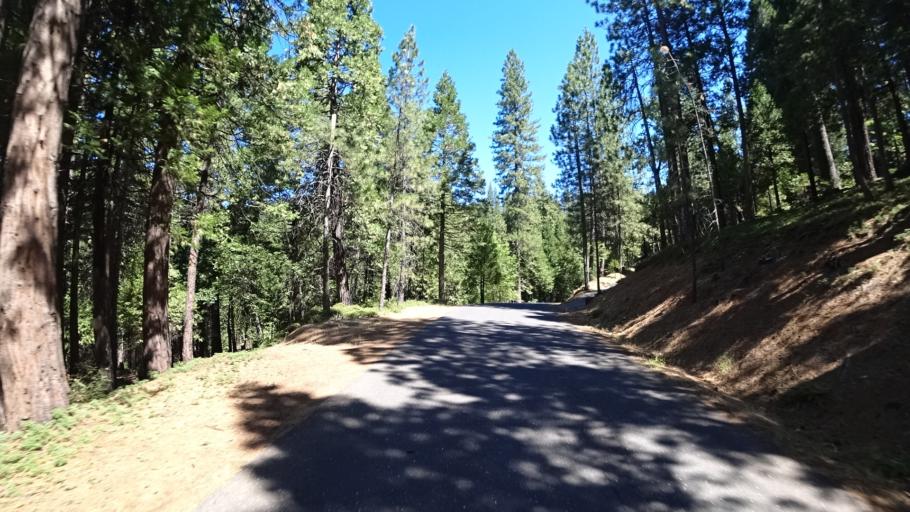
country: US
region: California
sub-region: Calaveras County
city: Arnold
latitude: 38.2365
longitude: -120.3325
